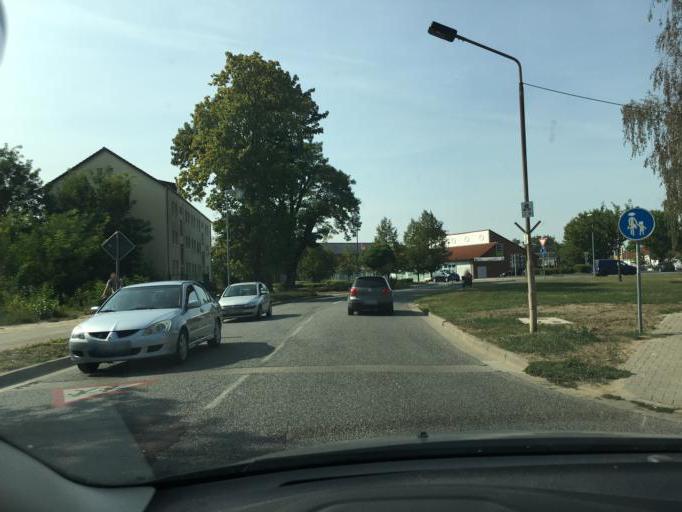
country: DE
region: Saxony-Anhalt
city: Calbe
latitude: 51.9114
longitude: 11.7779
